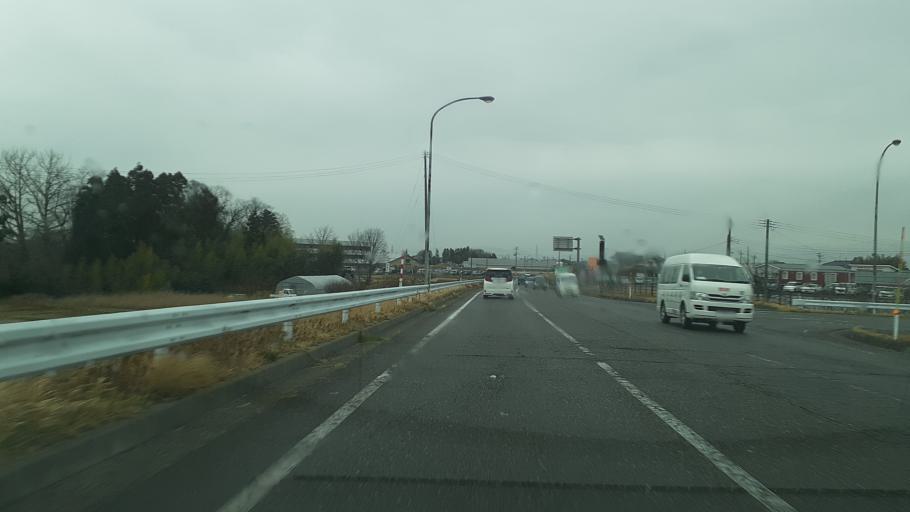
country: JP
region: Niigata
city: Kameda-honcho
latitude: 37.8821
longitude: 139.1705
